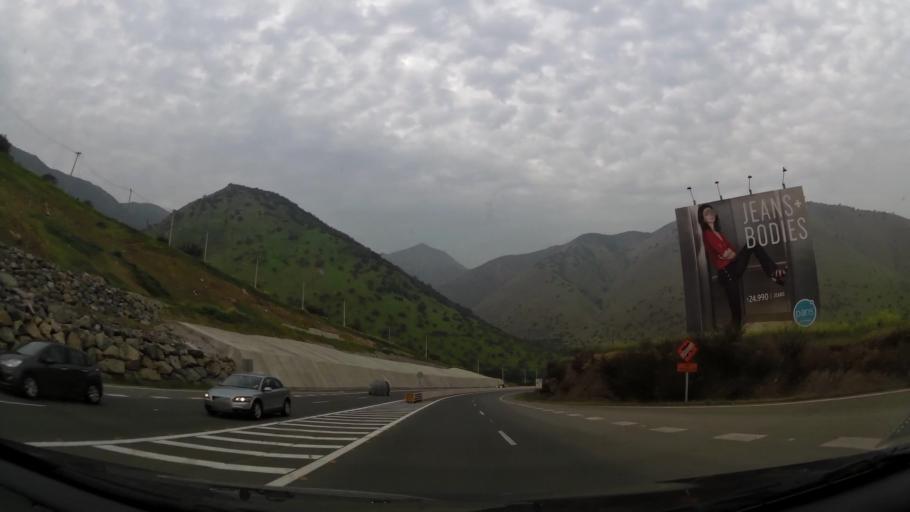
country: CL
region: Santiago Metropolitan
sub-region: Provincia de Chacabuco
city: Chicureo Abajo
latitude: -33.3521
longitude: -70.6183
